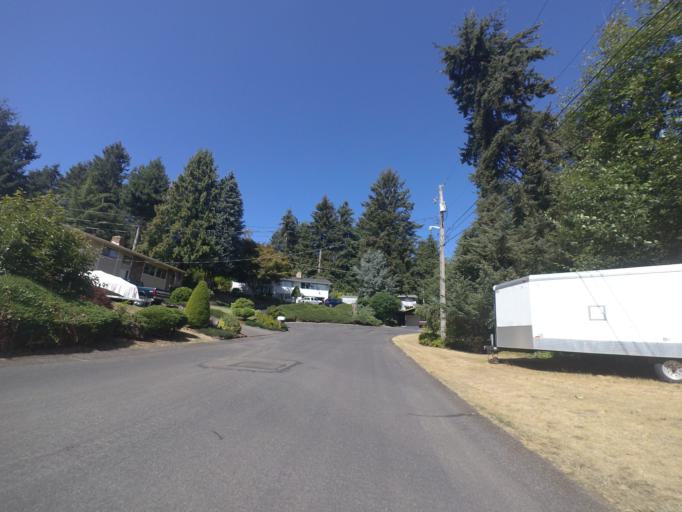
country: US
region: Washington
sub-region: Pierce County
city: Fircrest
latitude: 47.2167
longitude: -122.5139
